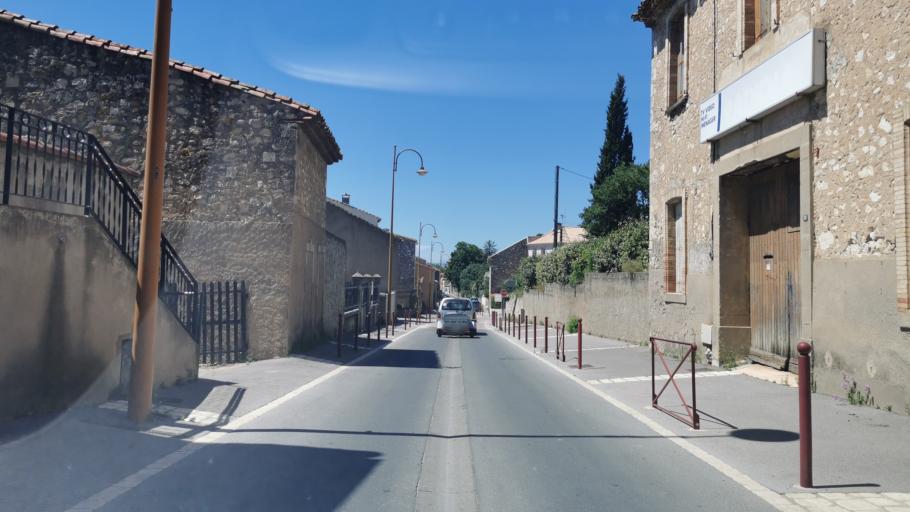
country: FR
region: Languedoc-Roussillon
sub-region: Departement de l'Aude
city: Fleury
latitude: 43.2352
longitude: 3.1211
